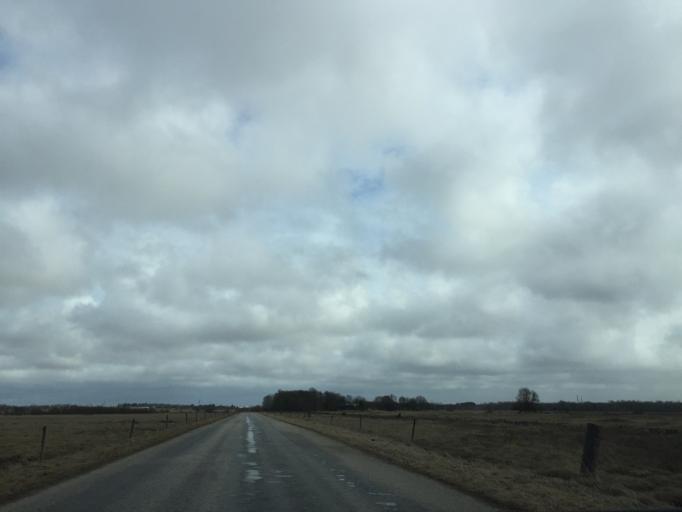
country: EE
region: Laeaene
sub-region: Lihula vald
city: Lihula
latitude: 58.7281
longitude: 23.8906
